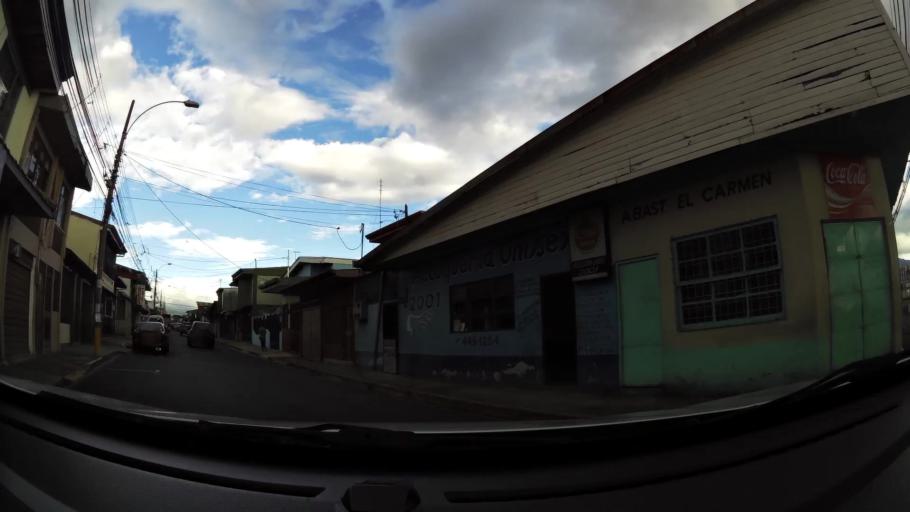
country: CR
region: Alajuela
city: Alajuela
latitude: 10.0129
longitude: -84.2159
